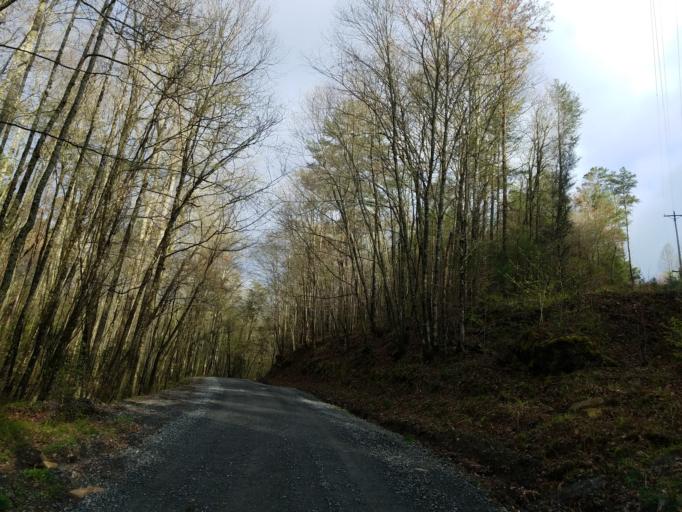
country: US
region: Georgia
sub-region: Fannin County
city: Blue Ridge
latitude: 34.7824
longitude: -84.2355
